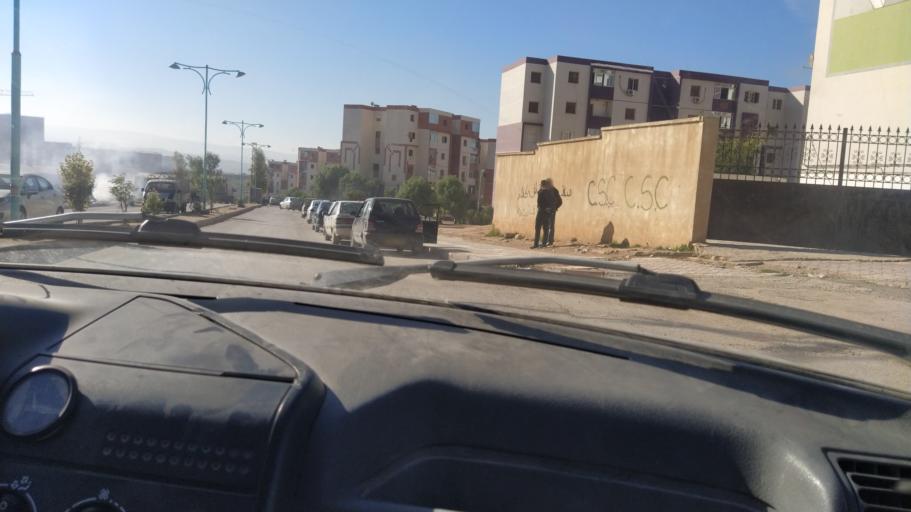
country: DZ
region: Constantine
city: Ain Smara
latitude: 36.2514
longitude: 6.5575
